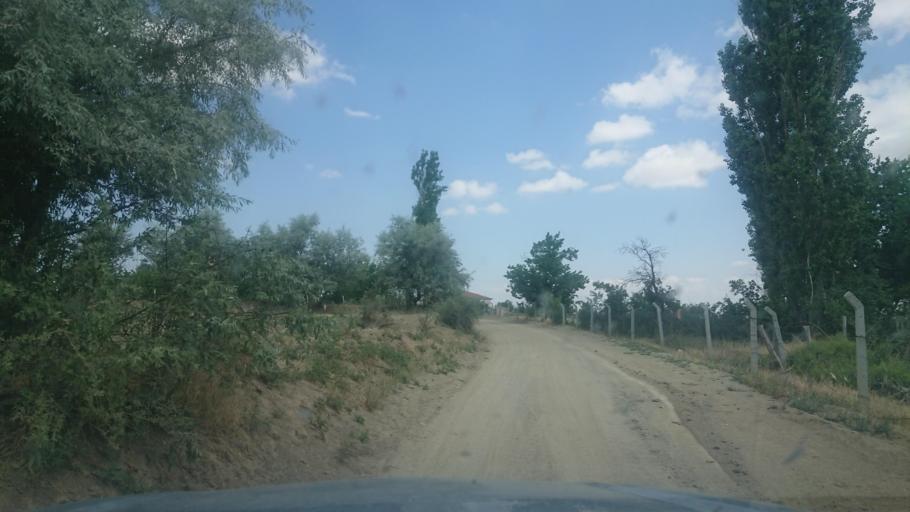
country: TR
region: Aksaray
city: Agacoren
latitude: 38.9335
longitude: 33.9528
